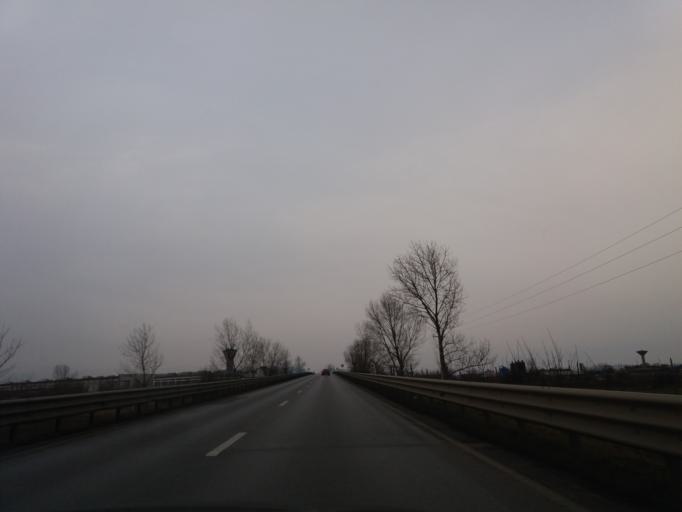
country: RO
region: Hunedoara
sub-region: Oras Simeria
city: Simeria
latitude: 45.8371
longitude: 23.0303
